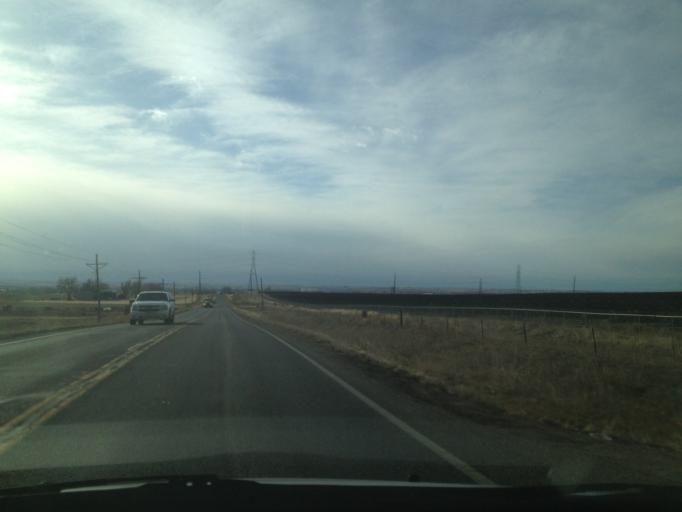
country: US
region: Colorado
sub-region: Weld County
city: Aristocrat Ranchettes
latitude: 40.0804
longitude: -104.7461
